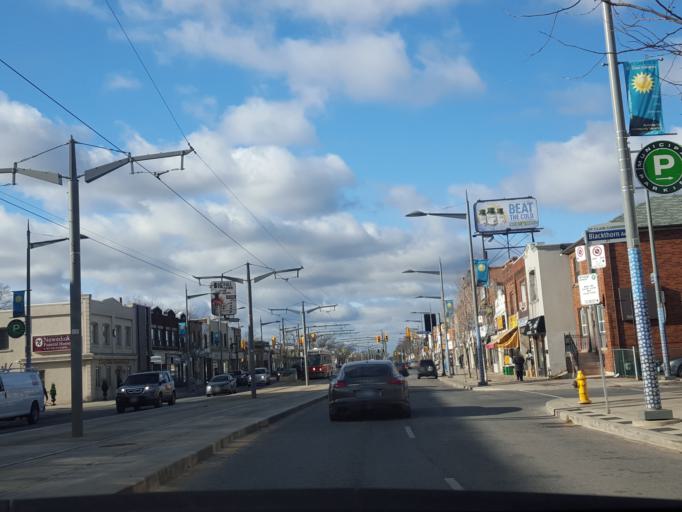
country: CA
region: Ontario
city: Toronto
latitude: 43.6746
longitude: -79.4583
